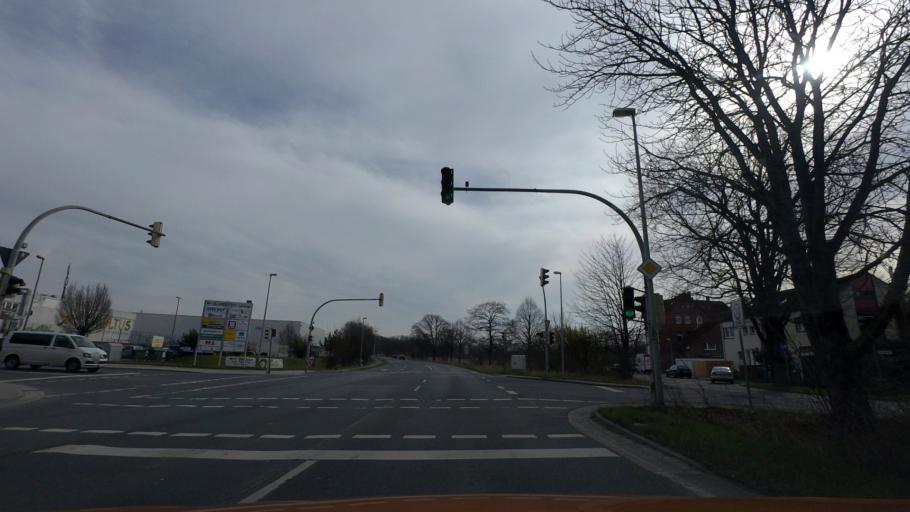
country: DE
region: Lower Saxony
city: Laatzen
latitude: 52.3665
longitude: 9.8620
